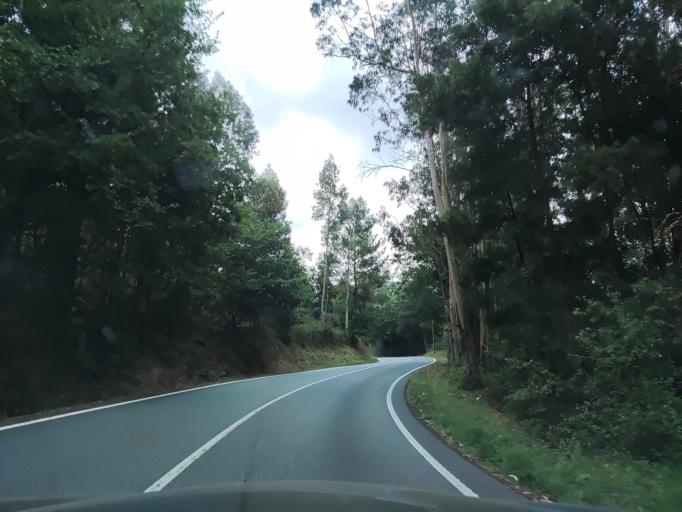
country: ES
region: Galicia
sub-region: Provincia da Coruna
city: Padron
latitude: 42.7463
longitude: -8.6195
